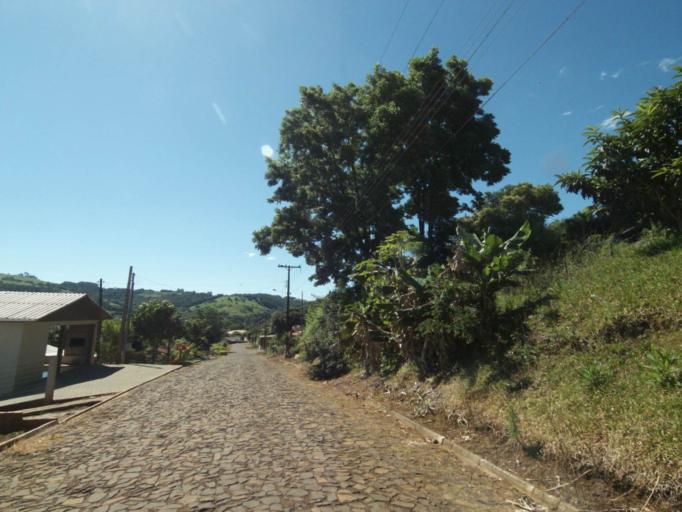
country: BR
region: Parana
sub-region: Ampere
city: Ampere
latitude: -26.1726
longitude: -53.3579
